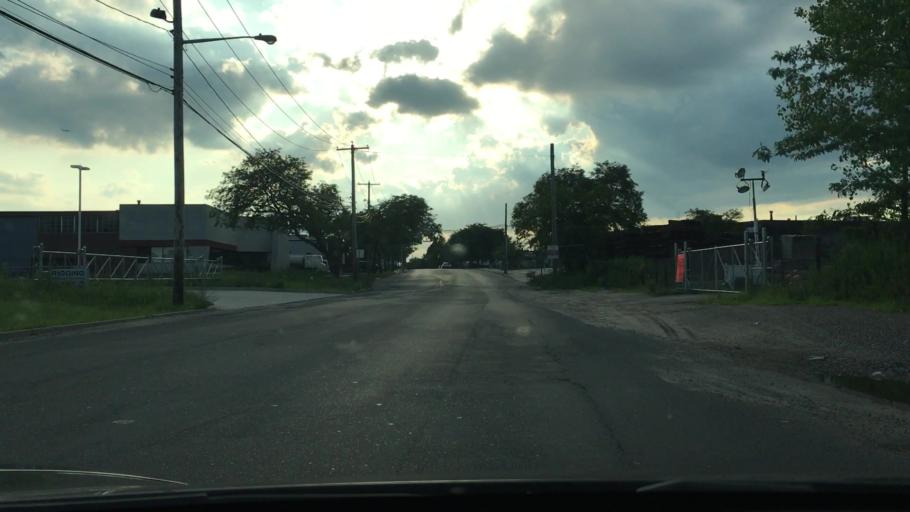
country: US
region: New York
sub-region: Suffolk County
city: Bay Wood
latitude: 40.7604
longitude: -73.2948
